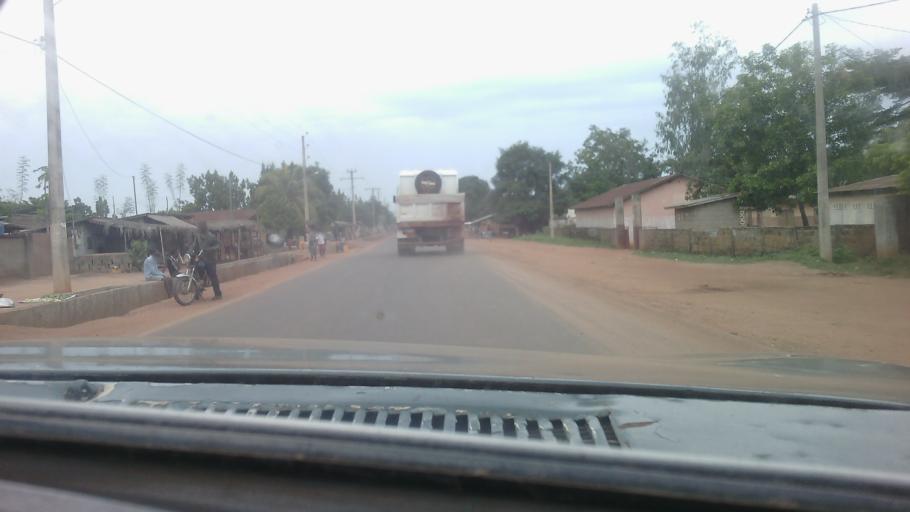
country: BJ
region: Mono
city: Come
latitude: 6.5132
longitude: 1.8248
